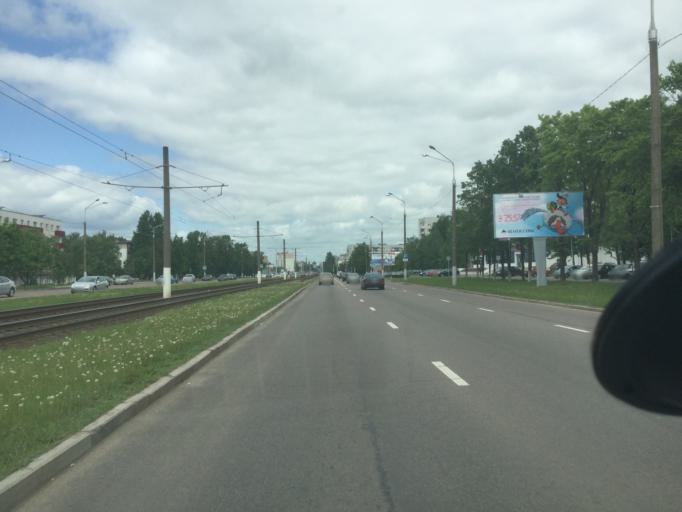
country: BY
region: Vitebsk
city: Vitebsk
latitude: 55.1810
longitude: 30.2299
